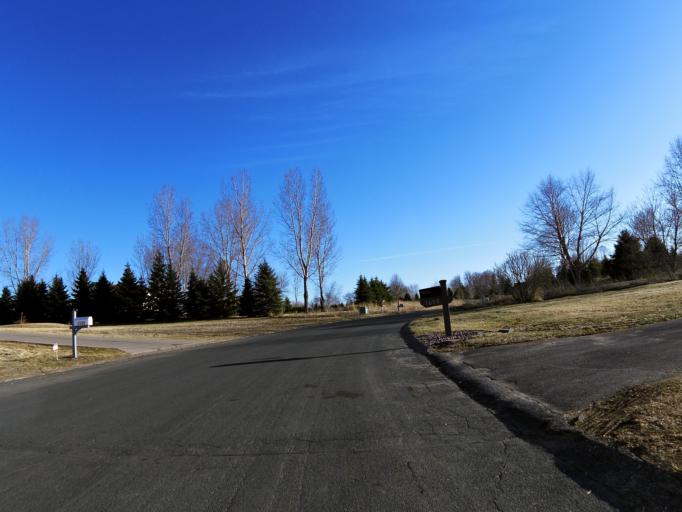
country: US
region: Minnesota
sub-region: Washington County
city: Lakeland
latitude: 44.9730
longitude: -92.8044
